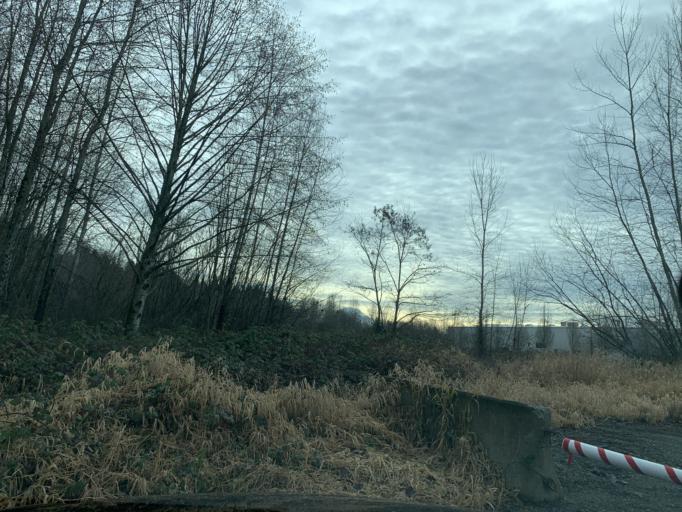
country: US
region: Washington
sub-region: Pierce County
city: Fife Heights
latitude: 47.2526
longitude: -122.3535
